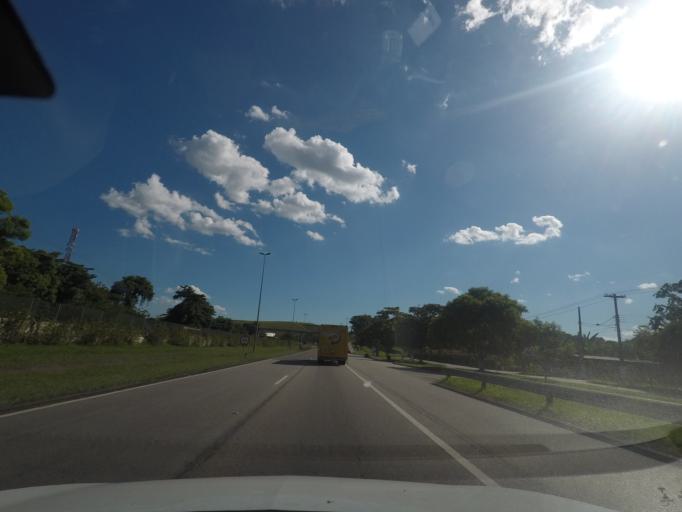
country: BR
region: Rio de Janeiro
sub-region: Guapimirim
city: Guapimirim
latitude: -22.5889
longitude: -43.0194
